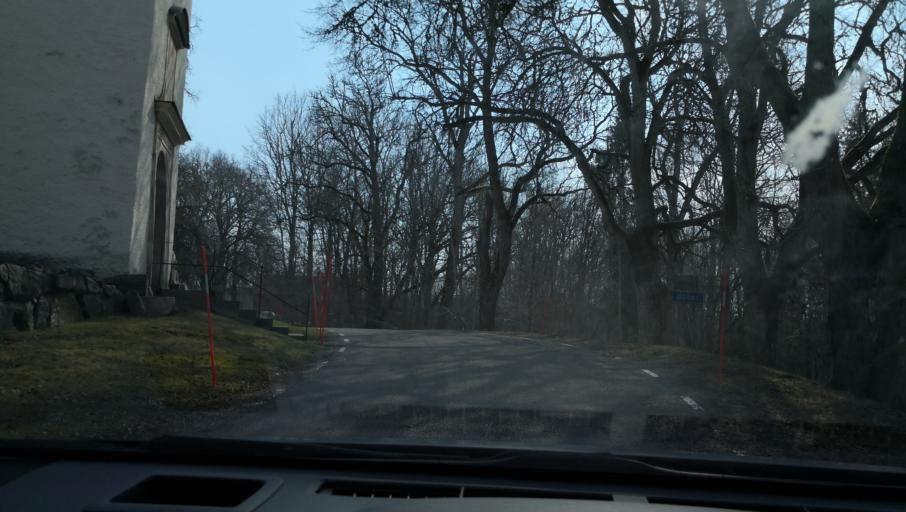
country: SE
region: OErebro
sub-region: Lindesbergs Kommun
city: Frovi
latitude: 59.4065
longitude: 15.4157
